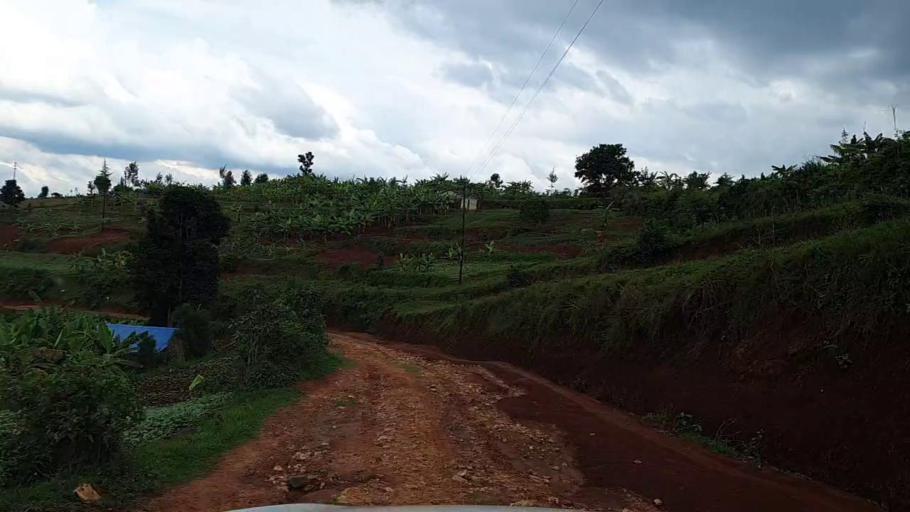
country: RW
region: Southern Province
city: Gikongoro
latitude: -2.4210
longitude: 29.6533
